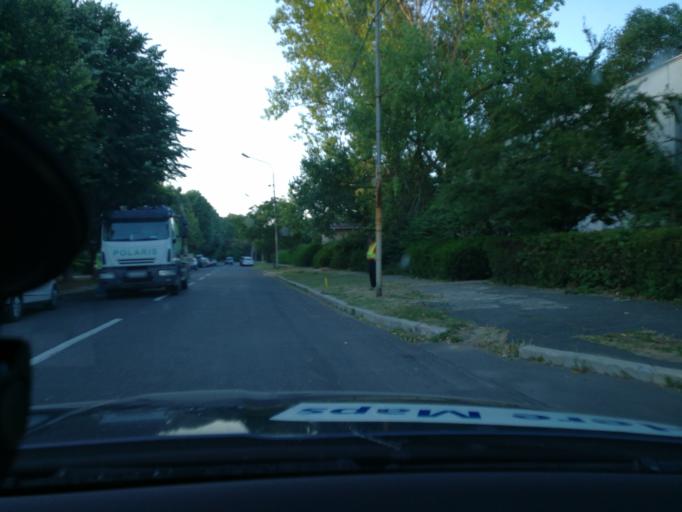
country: RO
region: Constanta
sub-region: Comuna Douazeci si Trei August
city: Douazeci si Trei August
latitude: 43.8737
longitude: 28.5999
